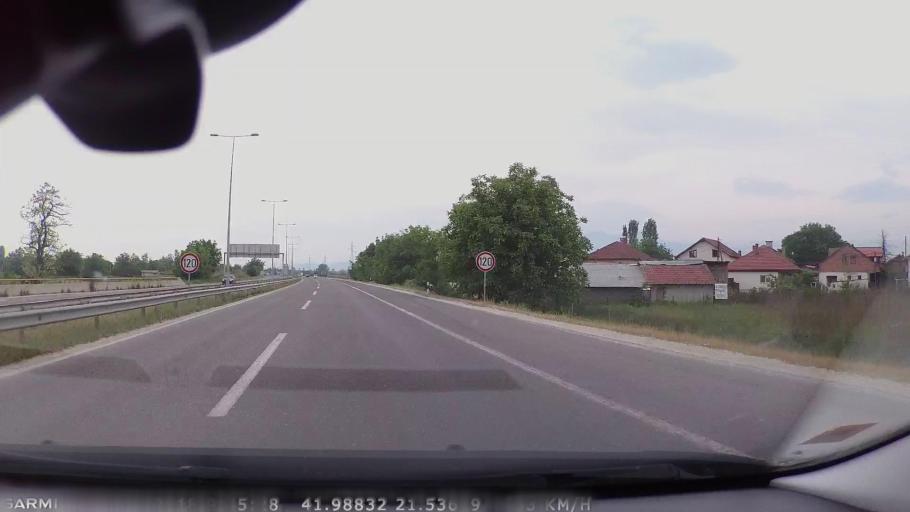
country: MK
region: Ilinden
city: Jurumleri
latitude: 41.9867
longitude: 21.5369
